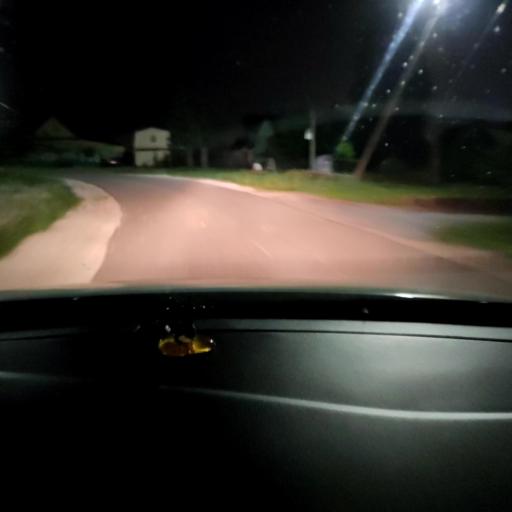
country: RU
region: Tatarstan
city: Stolbishchi
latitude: 55.6322
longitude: 49.1446
